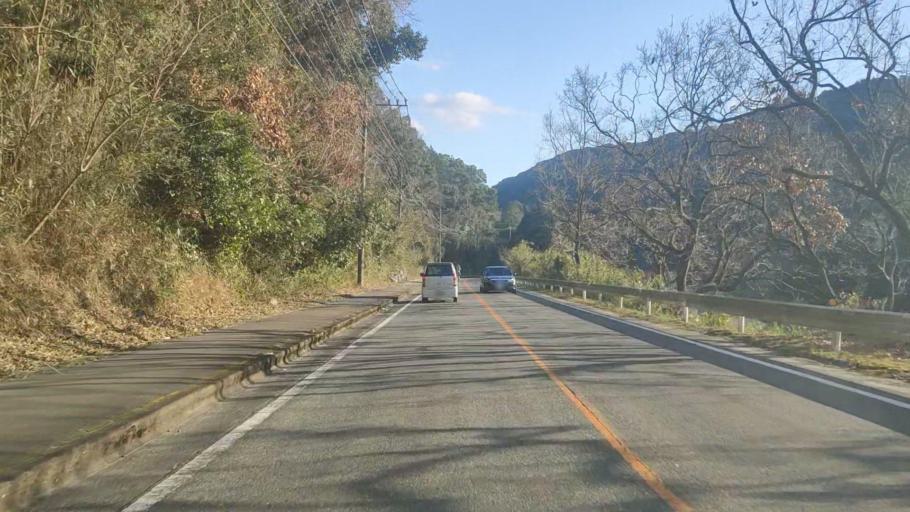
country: JP
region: Saga Prefecture
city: Saga-shi
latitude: 33.3355
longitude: 130.2617
